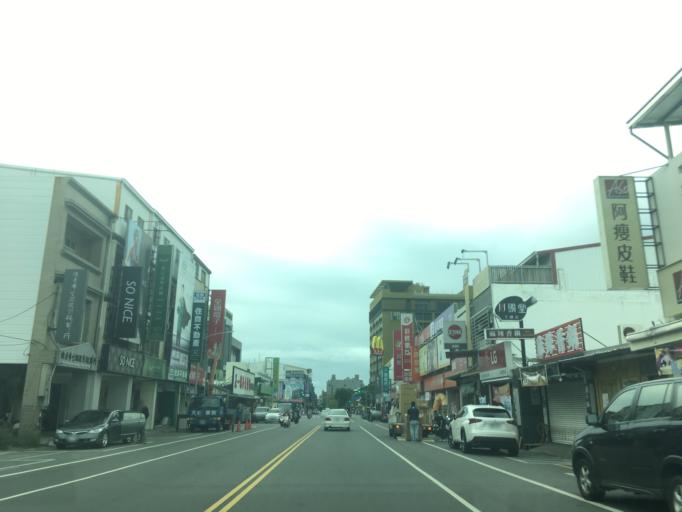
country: TW
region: Taiwan
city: Taitung City
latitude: 22.7563
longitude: 121.1440
